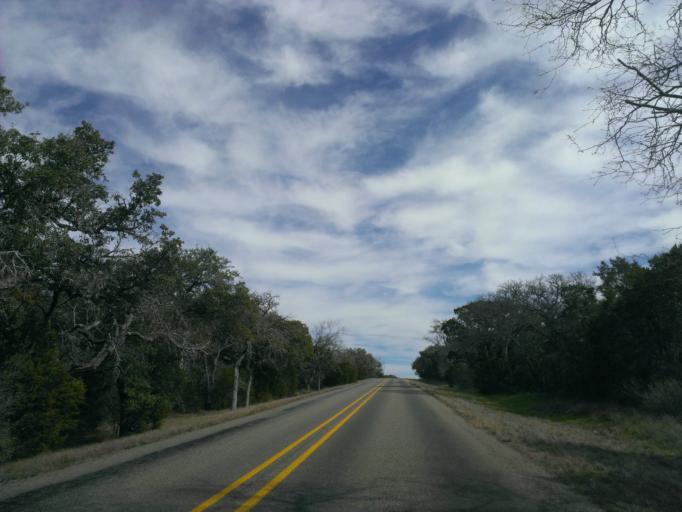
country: US
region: Texas
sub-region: Llano County
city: Buchanan Dam
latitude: 30.6965
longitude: -98.3655
